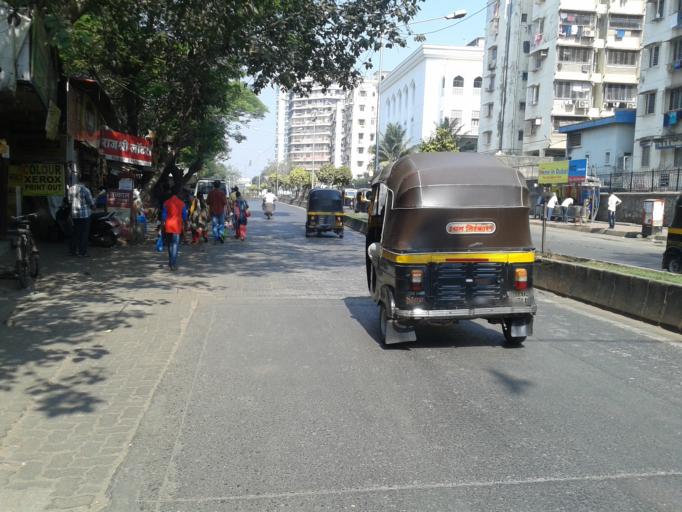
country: IN
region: Maharashtra
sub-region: Mumbai Suburban
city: Borivli
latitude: 19.2491
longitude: 72.8628
